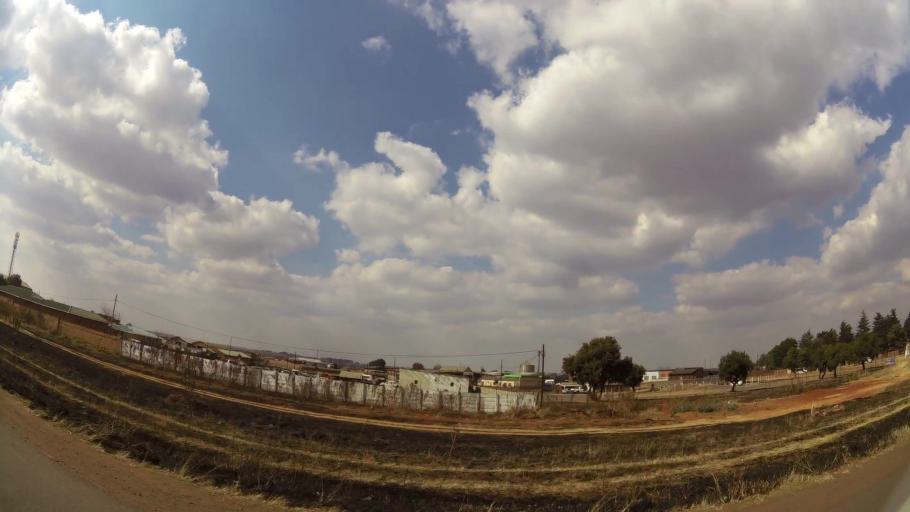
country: ZA
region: Mpumalanga
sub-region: Nkangala District Municipality
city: Delmas
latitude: -26.1325
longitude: 28.6843
